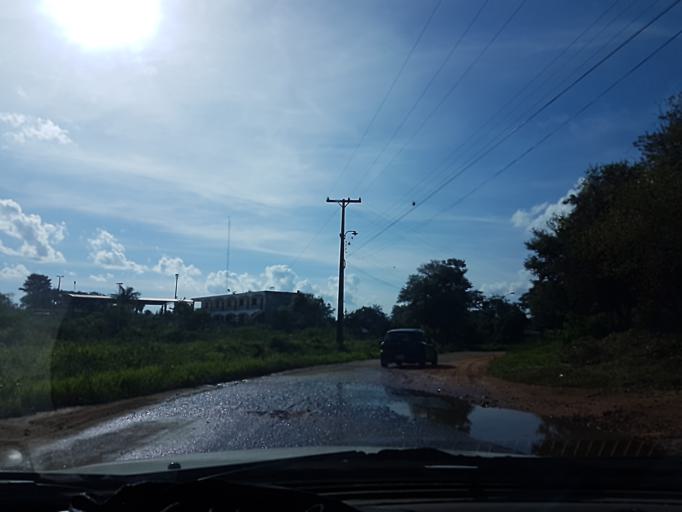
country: PY
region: Central
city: Limpio
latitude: -25.1963
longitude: -57.4585
